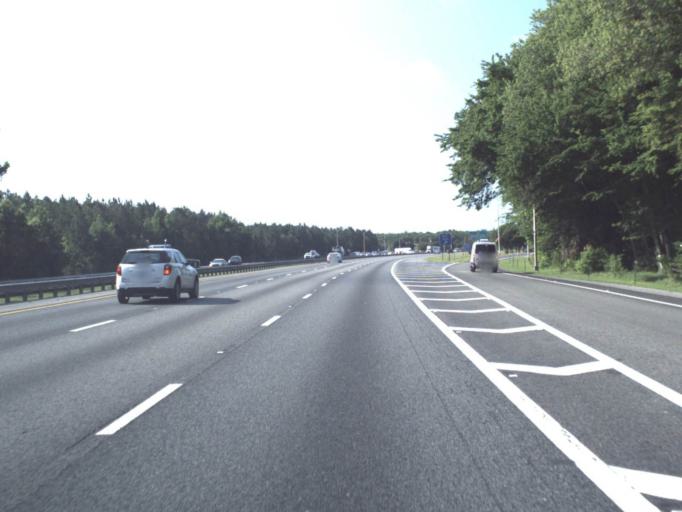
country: US
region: Florida
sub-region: Saint Johns County
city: Palm Valley
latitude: 30.0984
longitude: -81.4998
